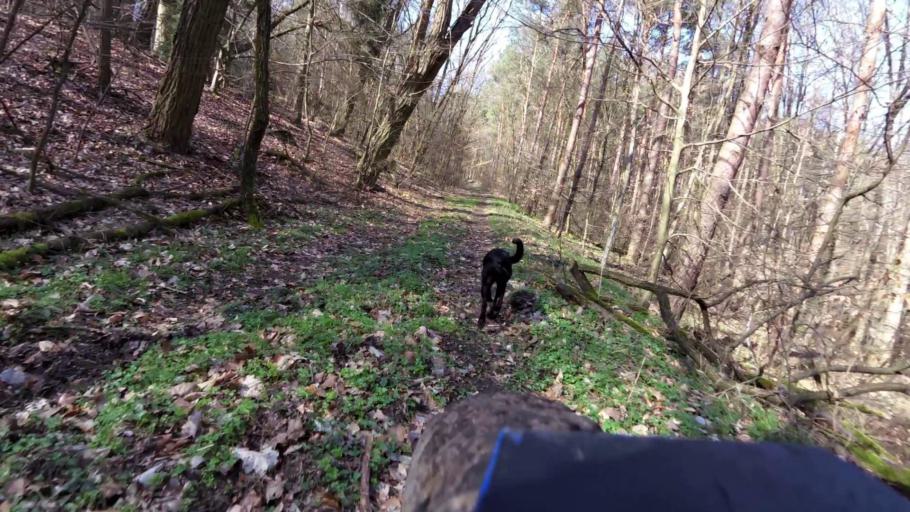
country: PL
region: Lubusz
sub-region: Powiat slubicki
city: Cybinka
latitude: 52.2086
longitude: 14.8713
